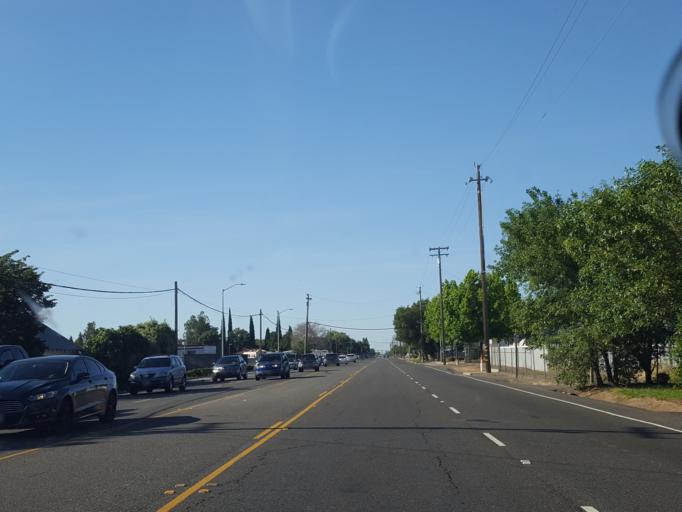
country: US
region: California
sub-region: Sacramento County
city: Florin
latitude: 38.4975
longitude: -121.3906
